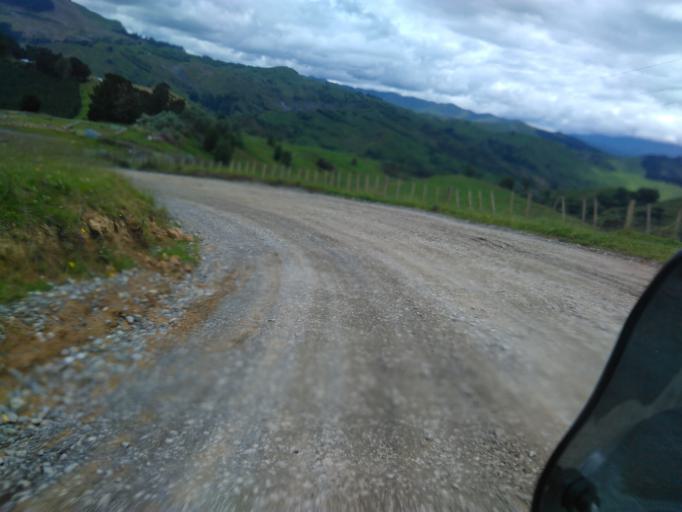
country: NZ
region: Gisborne
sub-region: Gisborne District
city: Gisborne
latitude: -38.0861
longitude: 178.0733
